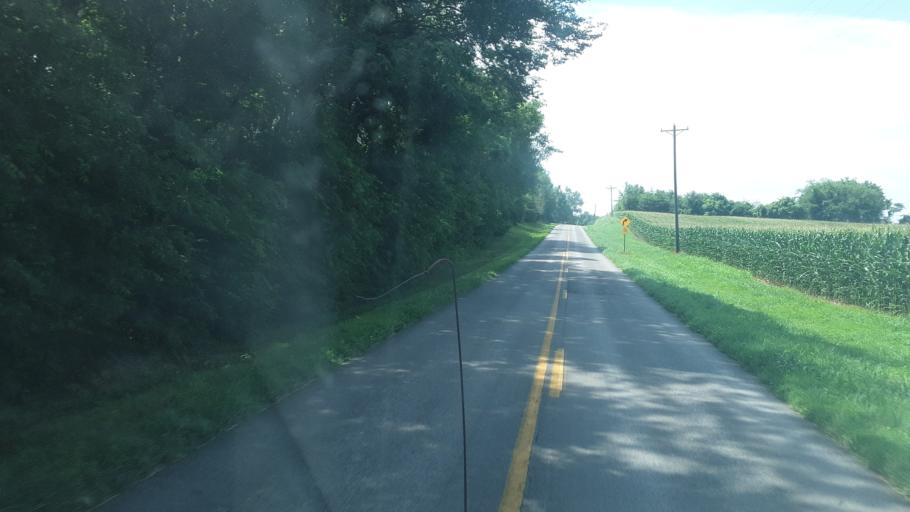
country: US
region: Kentucky
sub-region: Christian County
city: Oak Grove
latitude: 36.7350
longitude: -87.3216
